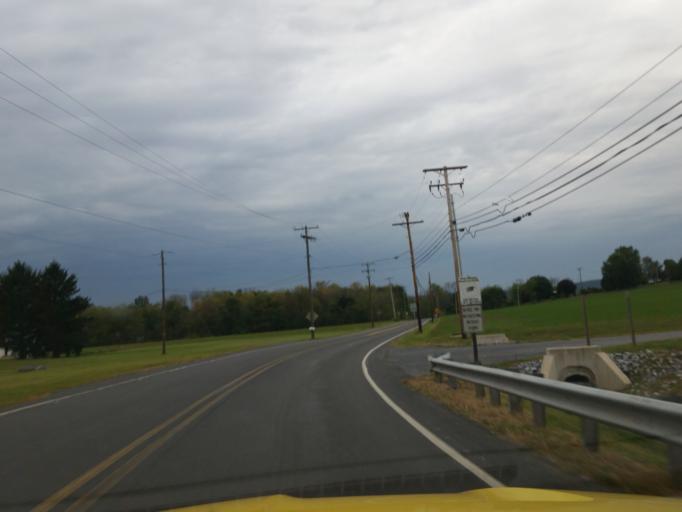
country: US
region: Pennsylvania
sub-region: Lebanon County
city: Myerstown
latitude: 40.4444
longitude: -76.3321
